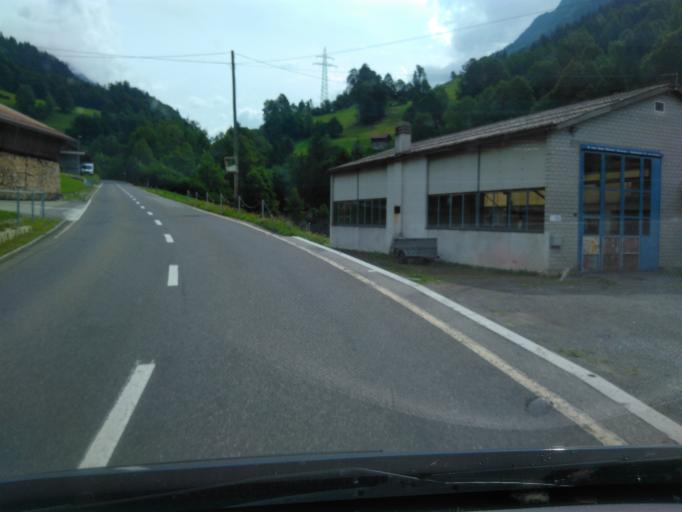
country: CH
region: Bern
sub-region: Interlaken-Oberhasli District
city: Meiringen
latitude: 46.7089
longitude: 8.2448
